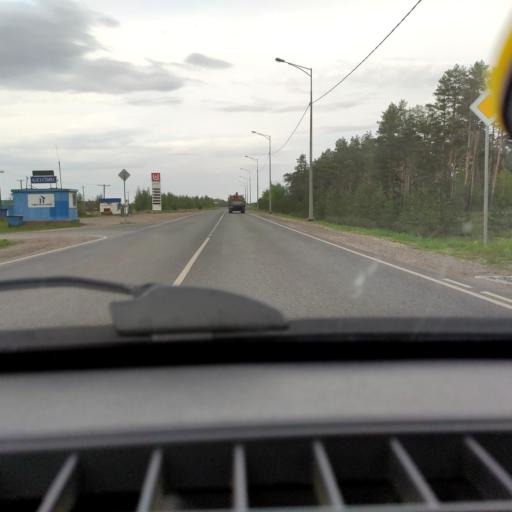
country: RU
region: Samara
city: Povolzhskiy
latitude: 53.5914
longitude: 49.5803
